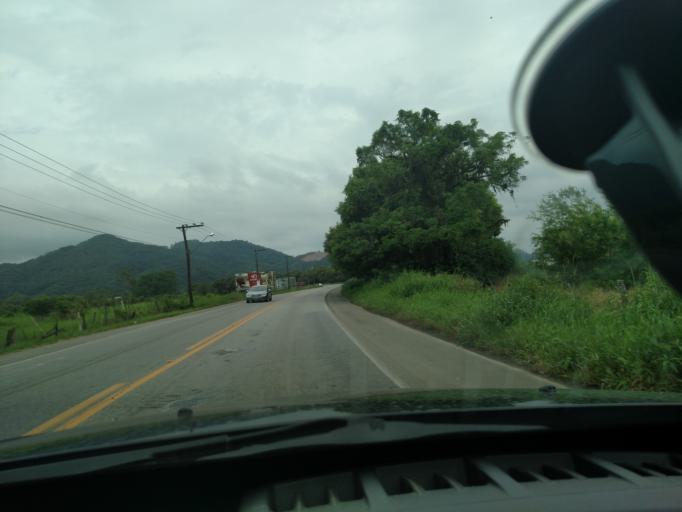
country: BR
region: Santa Catarina
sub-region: Itajai
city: Itajai
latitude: -26.8872
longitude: -48.7756
